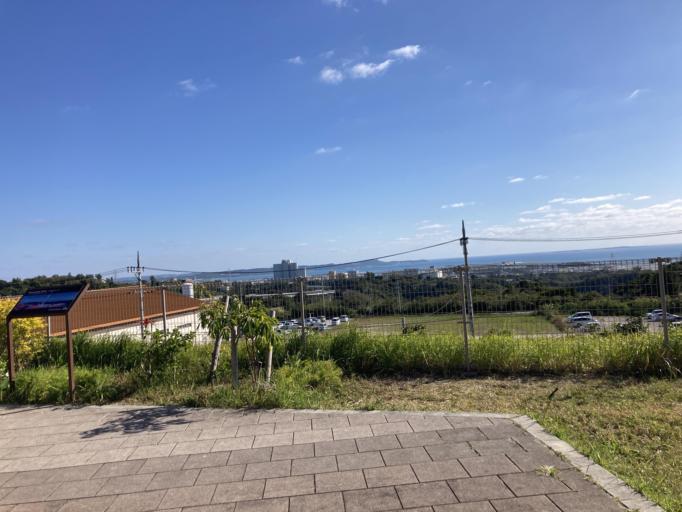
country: JP
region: Okinawa
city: Okinawa
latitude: 26.3144
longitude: 127.7980
